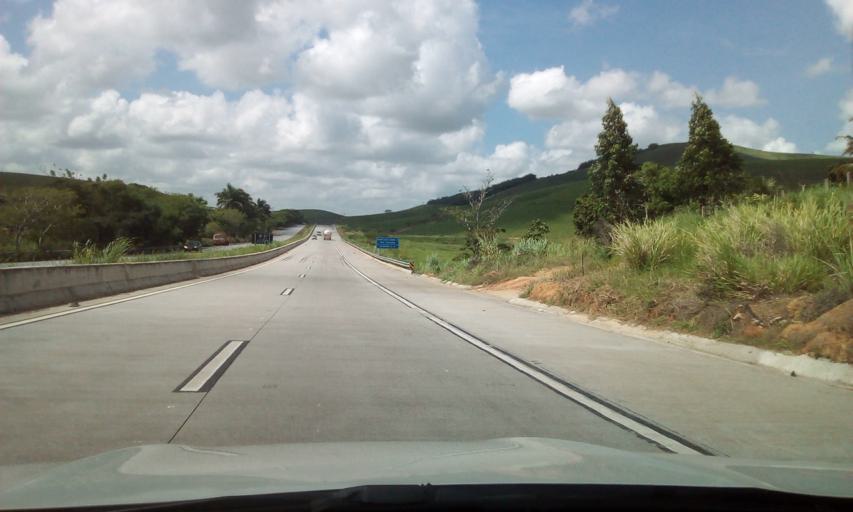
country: BR
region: Alagoas
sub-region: Flexeiras
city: Flexeiras
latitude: -9.2563
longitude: -35.7744
